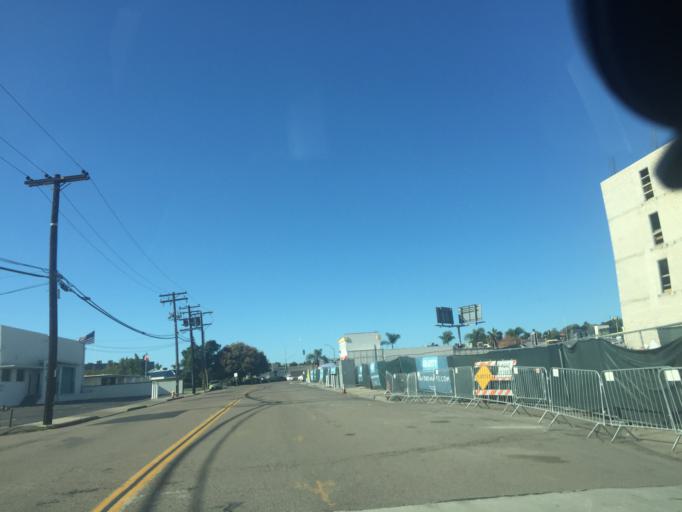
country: US
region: California
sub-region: San Diego County
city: La Mesa
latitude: 32.7830
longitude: -117.0966
